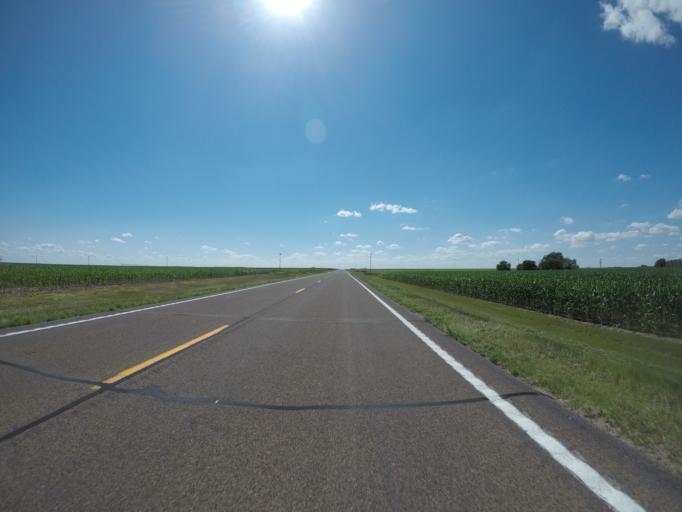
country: US
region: Nebraska
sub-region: Chase County
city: Imperial
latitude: 40.5373
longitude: -101.9476
